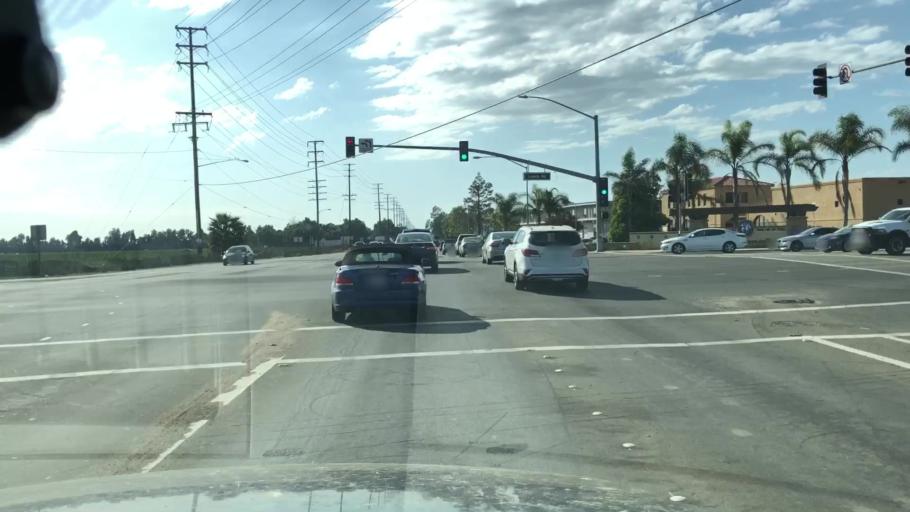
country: US
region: California
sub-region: Ventura County
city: Camarillo
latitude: 34.2055
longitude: -119.0343
